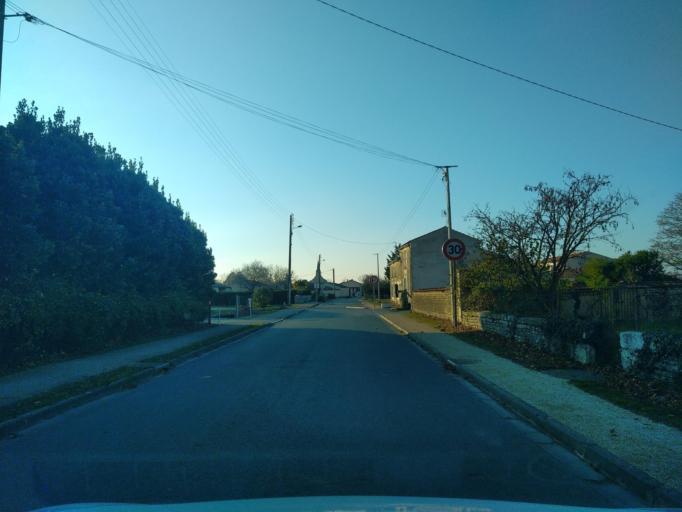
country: FR
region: Pays de la Loire
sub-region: Departement de la Vendee
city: Maillezais
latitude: 46.3419
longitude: -0.7848
